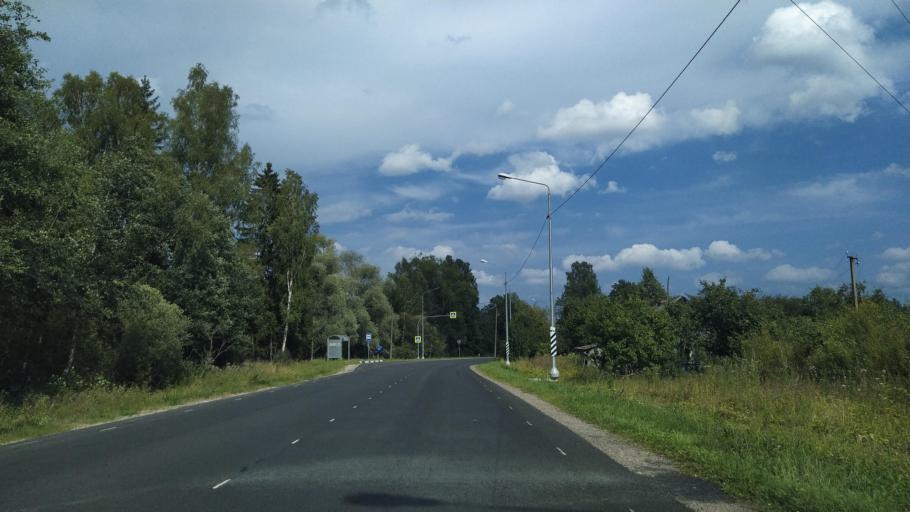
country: RU
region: Pskov
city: Vybor
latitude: 57.7310
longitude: 28.9737
